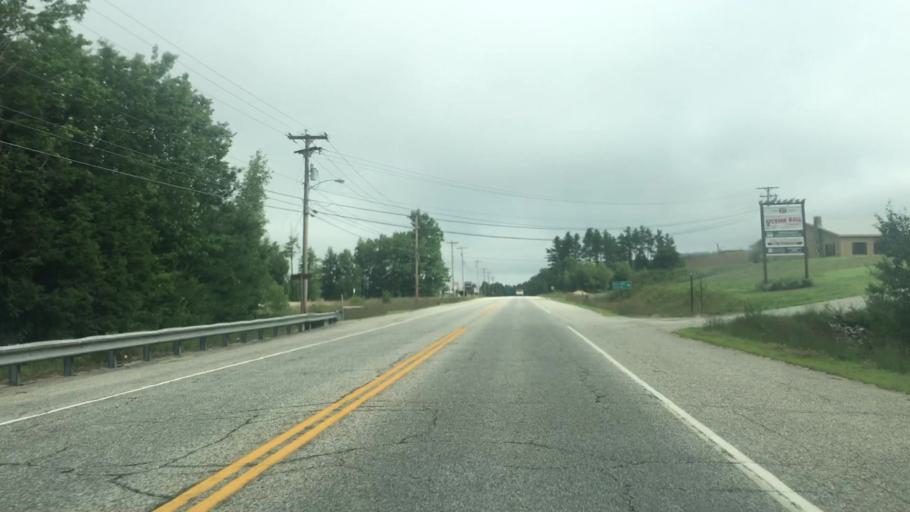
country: US
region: Maine
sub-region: Oxford County
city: South Paris
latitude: 44.2401
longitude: -70.5136
